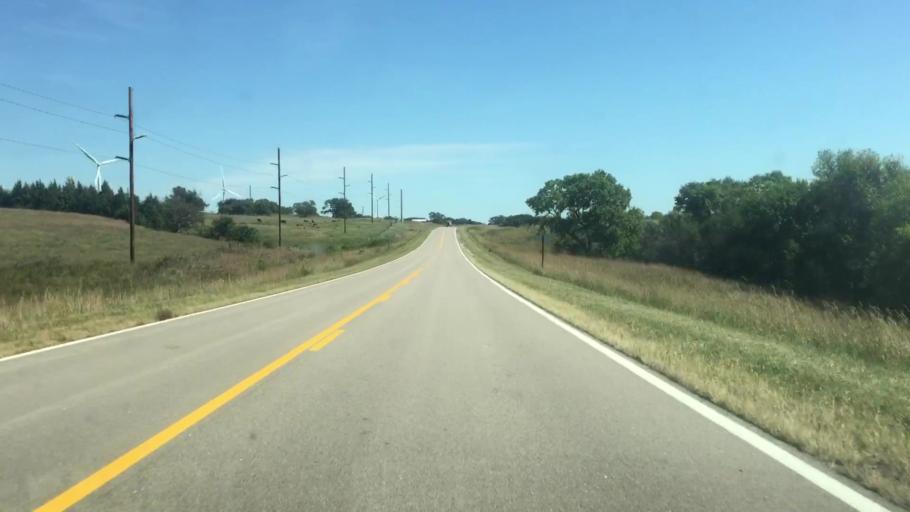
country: US
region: Nebraska
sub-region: Jefferson County
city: Fairbury
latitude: 40.0450
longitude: -96.9600
